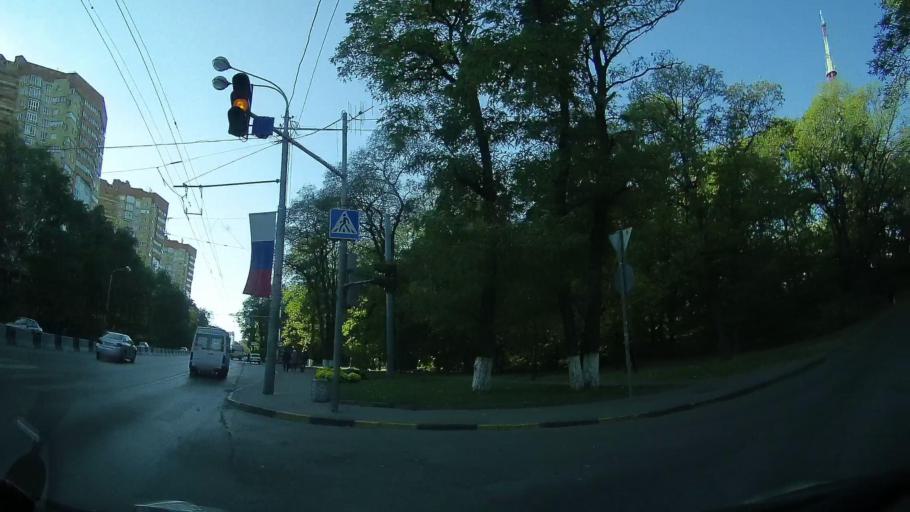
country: RU
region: Rostov
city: Rostov-na-Donu
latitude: 47.2112
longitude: 39.6797
